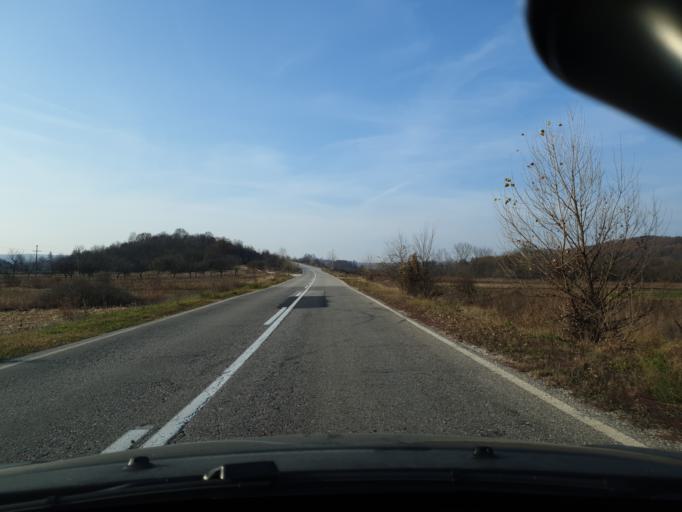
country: RS
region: Central Serbia
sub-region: Zajecarski Okrug
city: Zajecar
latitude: 43.9549
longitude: 22.2780
